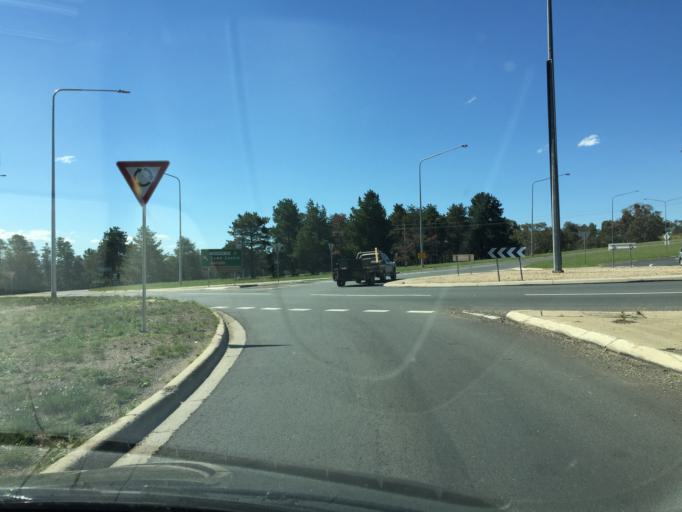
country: AU
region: Australian Capital Territory
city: Macarthur
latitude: -35.4366
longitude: 149.1255
